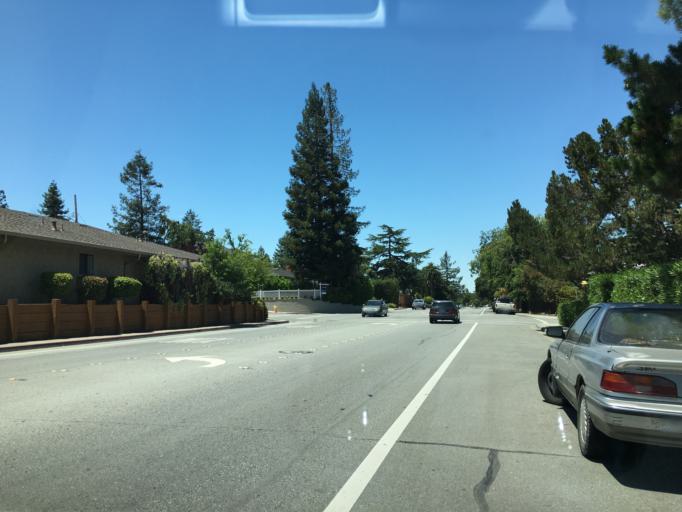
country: US
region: California
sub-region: San Mateo County
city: West Menlo Park
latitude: 37.4329
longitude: -122.2036
